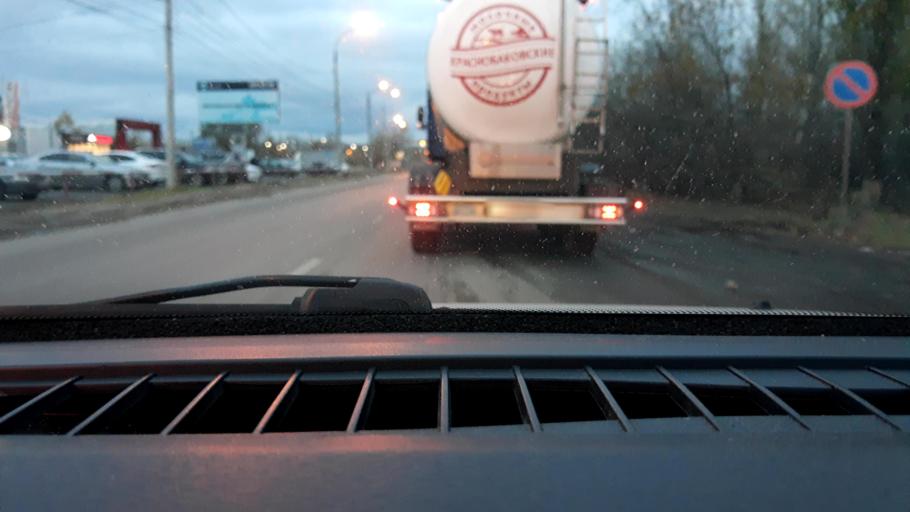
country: RU
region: Nizjnij Novgorod
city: Gorbatovka
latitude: 56.3526
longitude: 43.8029
